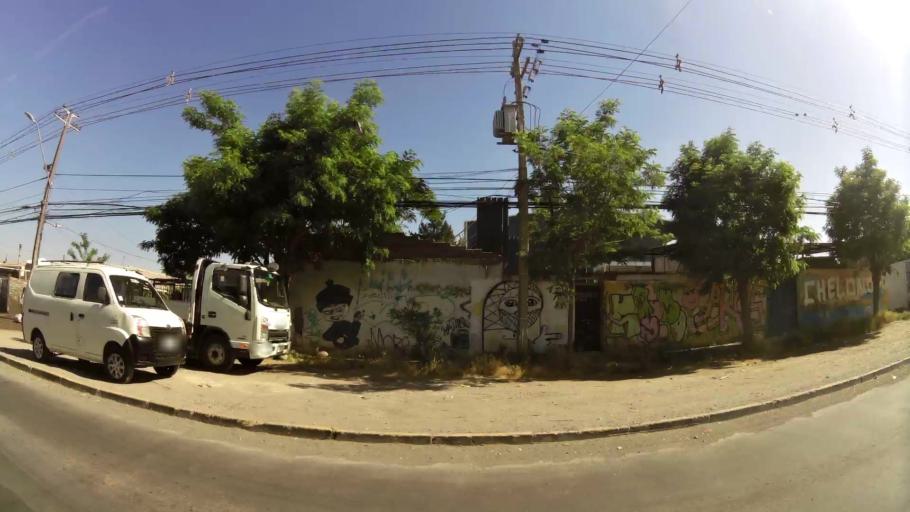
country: CL
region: Santiago Metropolitan
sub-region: Provincia de Maipo
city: San Bernardo
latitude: -33.5667
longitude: -70.7006
